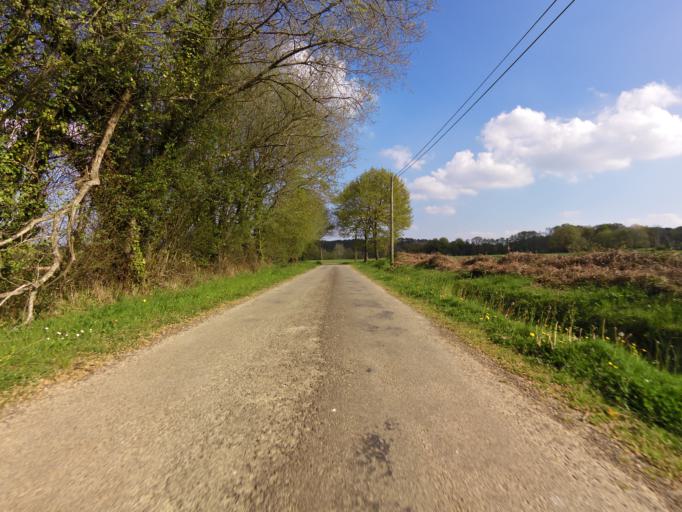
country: FR
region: Brittany
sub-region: Departement du Morbihan
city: Pluherlin
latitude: 47.7103
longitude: -2.3413
